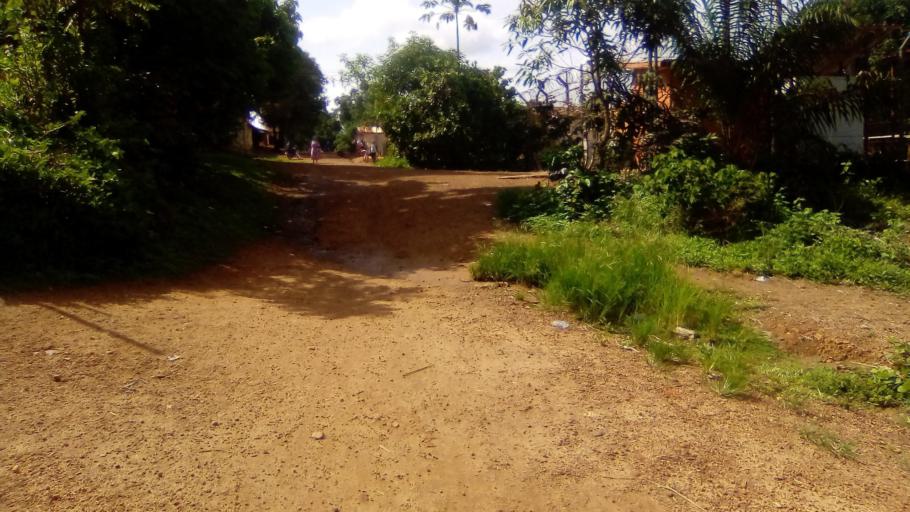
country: SL
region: Southern Province
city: Bo
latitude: 7.9775
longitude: -11.7290
